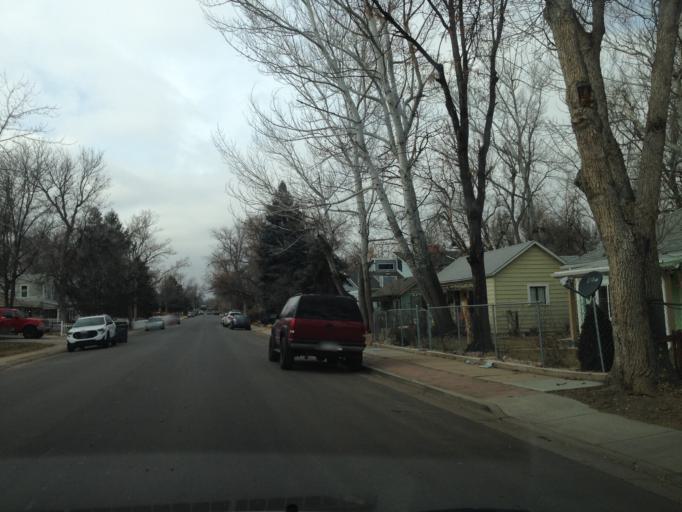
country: US
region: Colorado
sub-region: Boulder County
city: Lafayette
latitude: 39.9942
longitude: -105.0821
